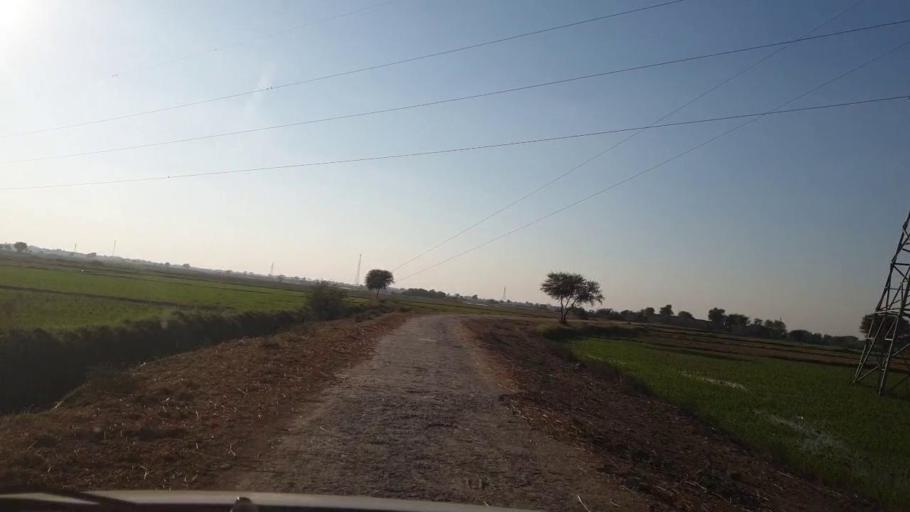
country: PK
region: Sindh
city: Khairpur Nathan Shah
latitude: 27.0414
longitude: 67.7309
